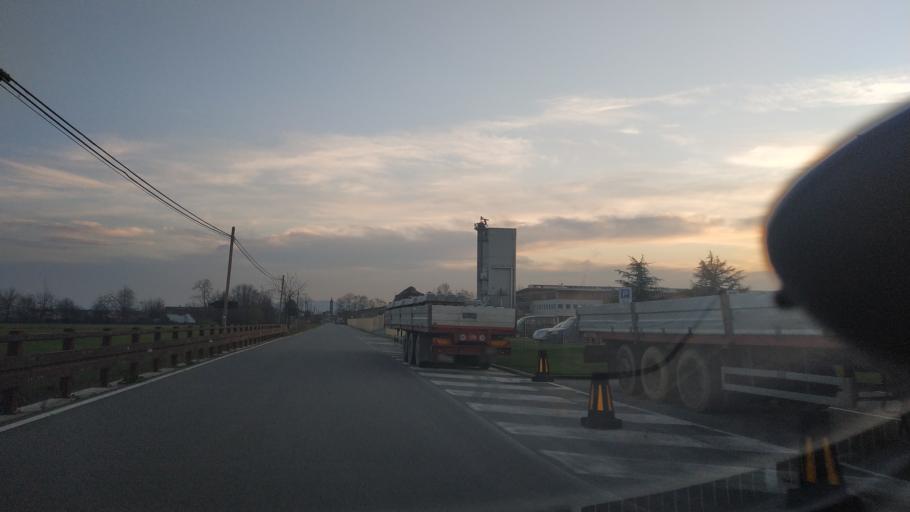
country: IT
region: Piedmont
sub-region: Provincia di Torino
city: Caluso
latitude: 45.2733
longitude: 7.8780
